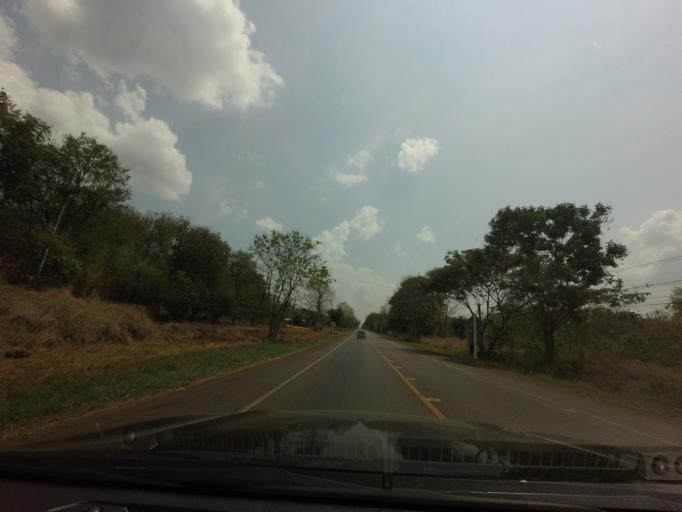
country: TH
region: Kanchanaburi
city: Sai Yok
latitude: 14.1346
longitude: 99.1550
